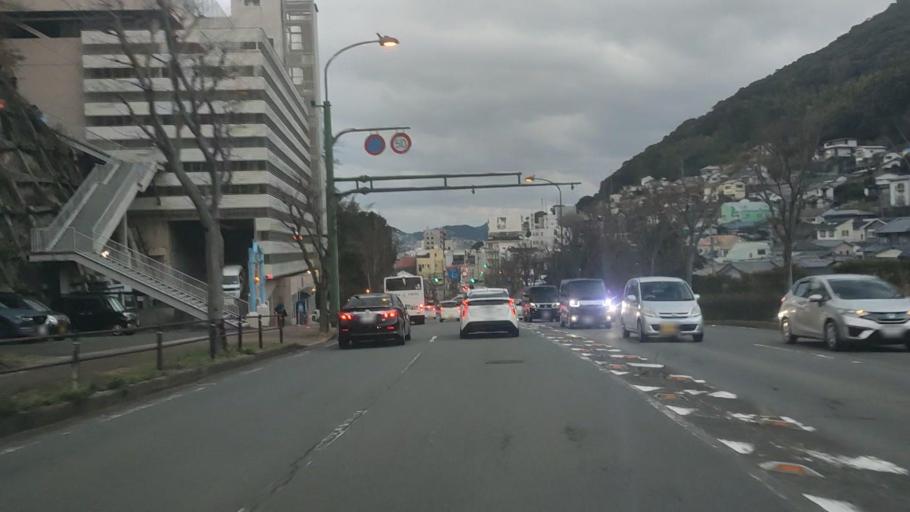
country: JP
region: Nagasaki
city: Nagasaki-shi
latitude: 32.7655
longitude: 129.8902
